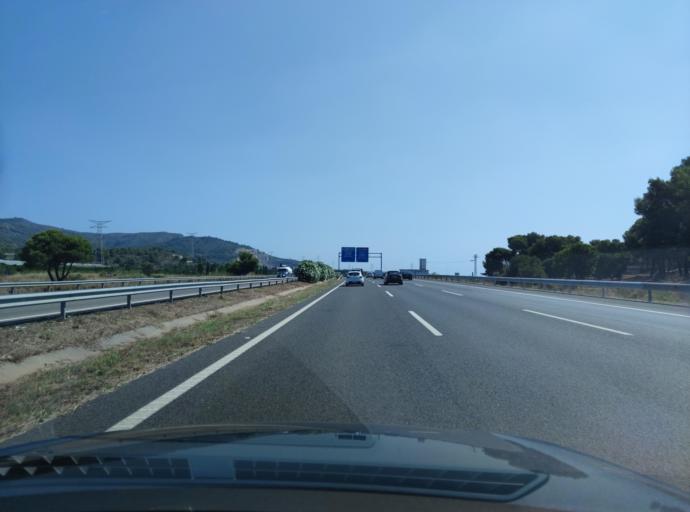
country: ES
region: Valencia
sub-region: Provincia de Valencia
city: Petres
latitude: 39.6883
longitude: -0.2887
